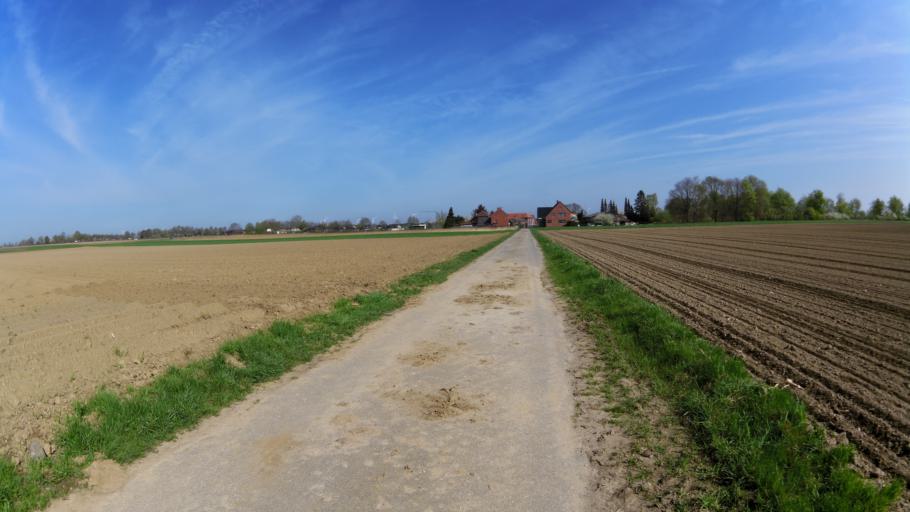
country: DE
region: North Rhine-Westphalia
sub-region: Regierungsbezirk Koln
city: Gangelt
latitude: 50.9980
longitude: 6.0339
